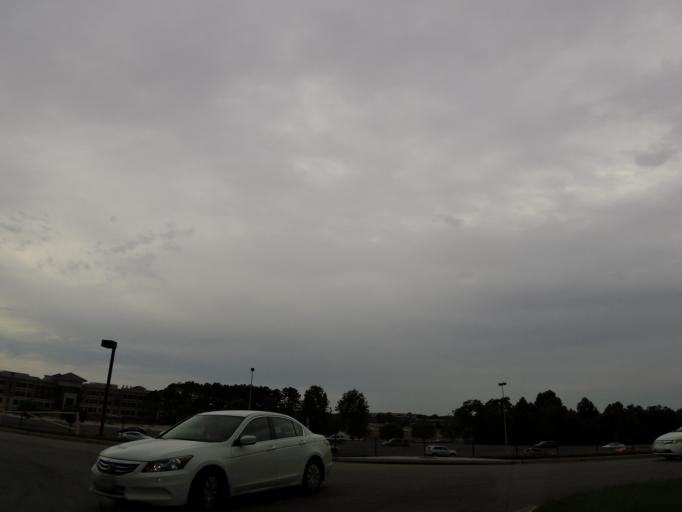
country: US
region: Alabama
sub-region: Madison County
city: Redstone Arsenal
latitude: 34.7123
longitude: -86.6532
